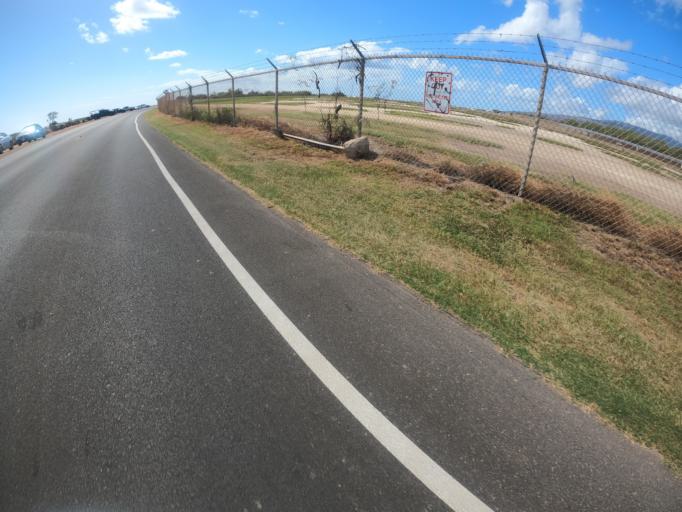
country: US
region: Hawaii
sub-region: Honolulu County
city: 'Ewa Villages
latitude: 21.3009
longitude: -158.0600
